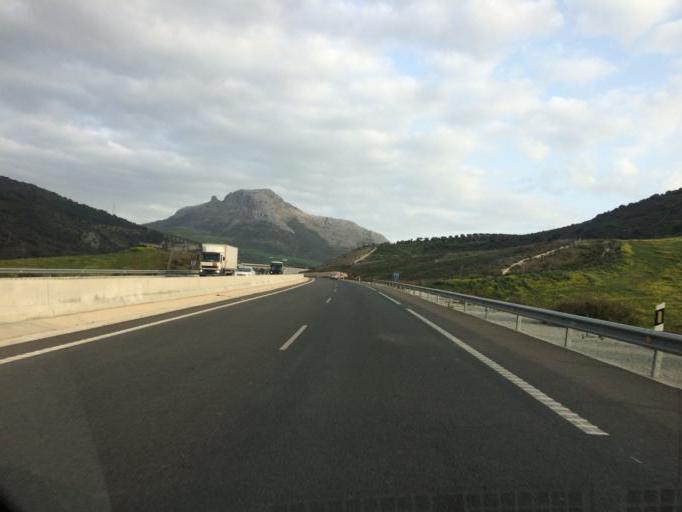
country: ES
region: Andalusia
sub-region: Provincia de Malaga
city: Casabermeja
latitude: 36.9395
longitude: -4.4333
